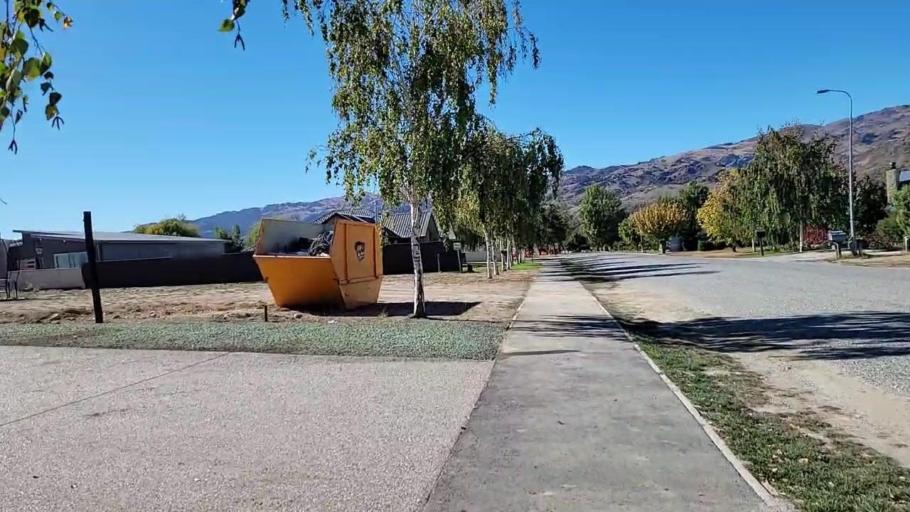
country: NZ
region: Otago
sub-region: Queenstown-Lakes District
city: Wanaka
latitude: -44.9776
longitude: 169.2381
